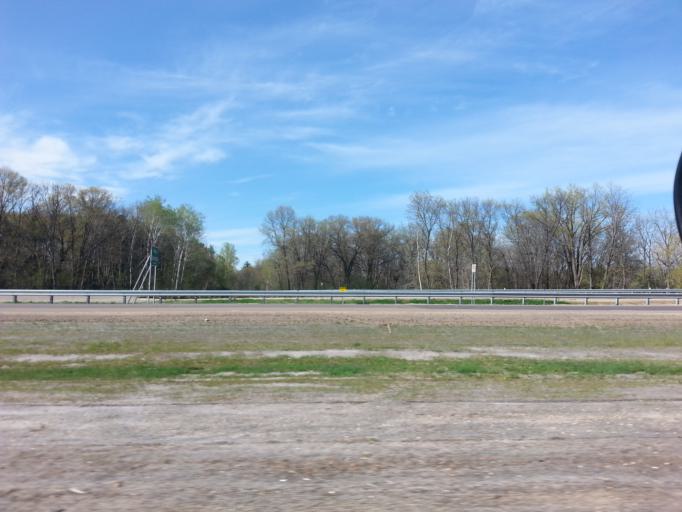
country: US
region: Minnesota
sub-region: Washington County
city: Mahtomedi
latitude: 45.0358
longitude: -92.9449
